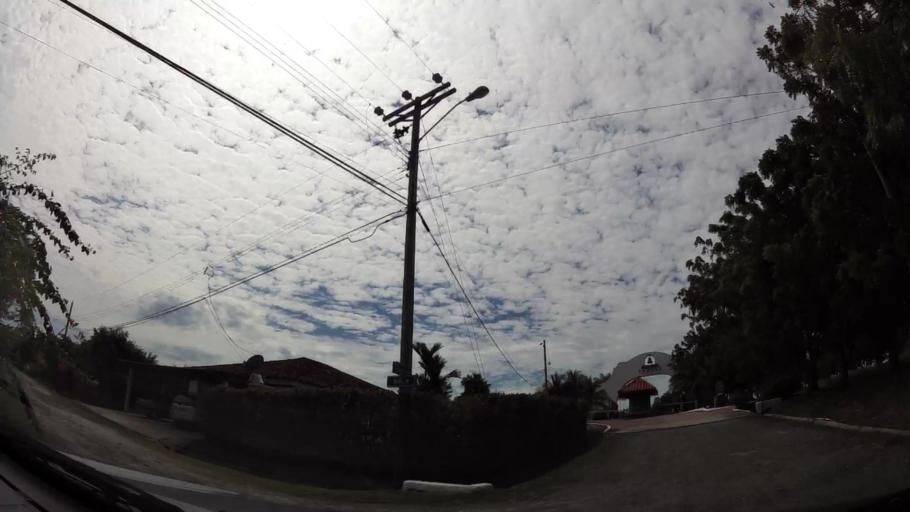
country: PA
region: Panama
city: Nueva Gorgona
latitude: 8.5393
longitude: -79.9067
